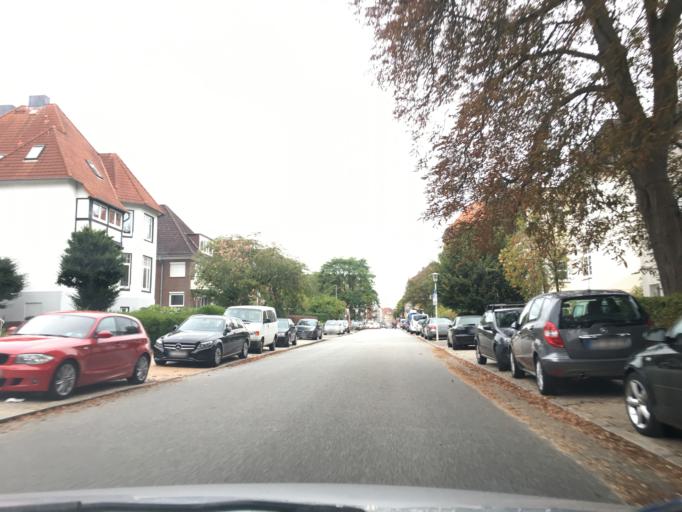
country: DE
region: Schleswig-Holstein
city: Kiel
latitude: 54.3353
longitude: 10.1422
